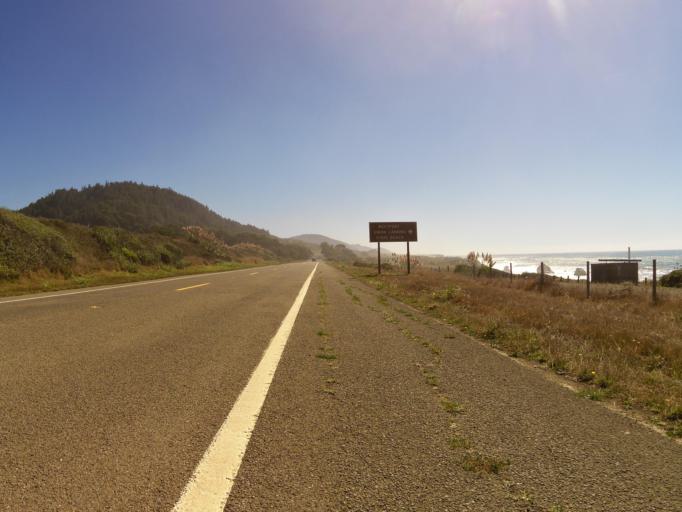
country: US
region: California
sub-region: Mendocino County
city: Fort Bragg
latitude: 39.6825
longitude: -123.7911
